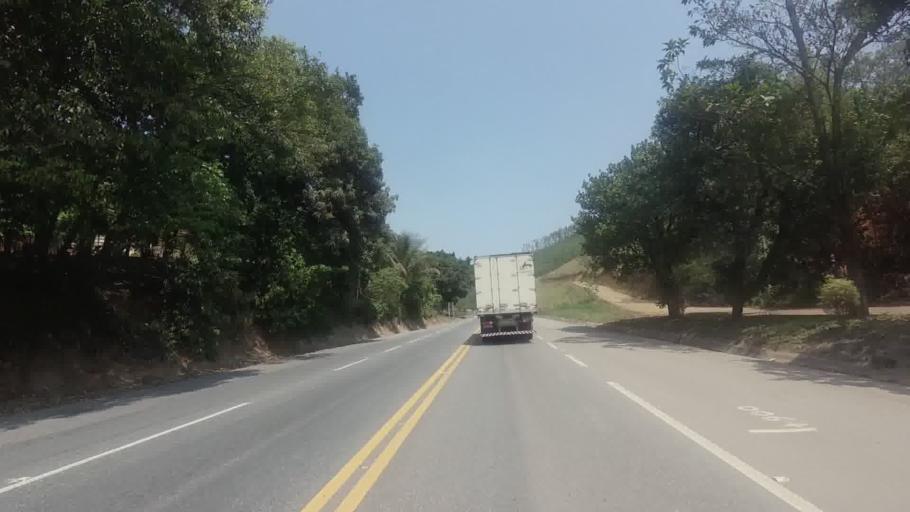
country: BR
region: Espirito Santo
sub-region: Iconha
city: Iconha
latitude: -20.8238
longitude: -40.8524
